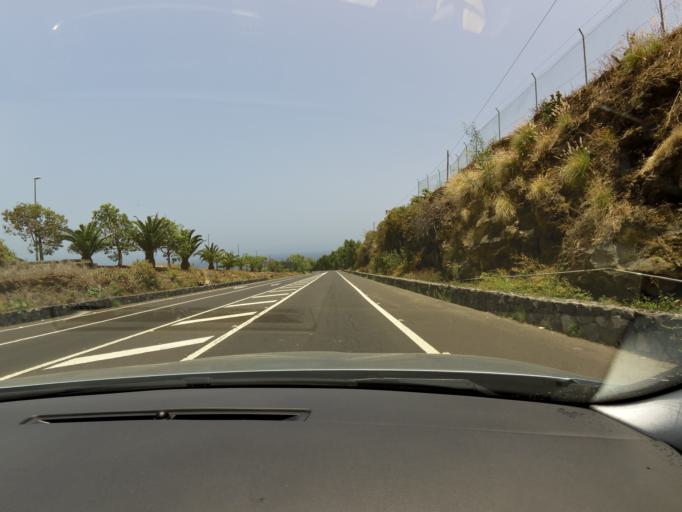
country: ES
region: Canary Islands
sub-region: Provincia de Santa Cruz de Tenerife
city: Puerto de la Cruz
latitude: 28.4130
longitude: -16.5291
